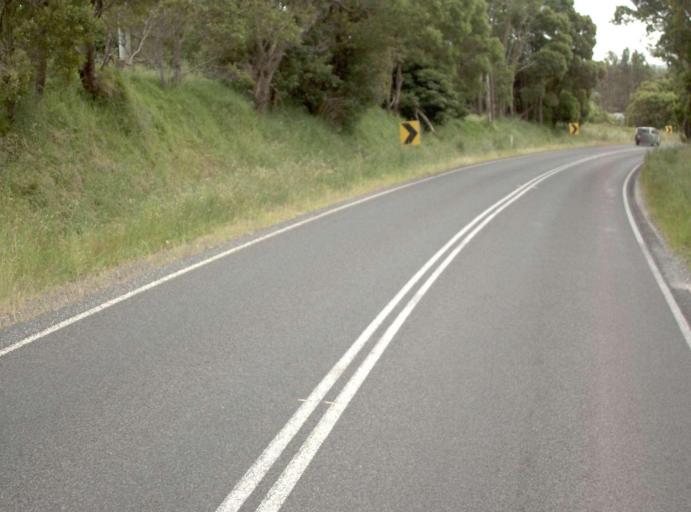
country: AU
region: Victoria
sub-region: Bass Coast
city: North Wonthaggi
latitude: -38.4699
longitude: 145.7715
